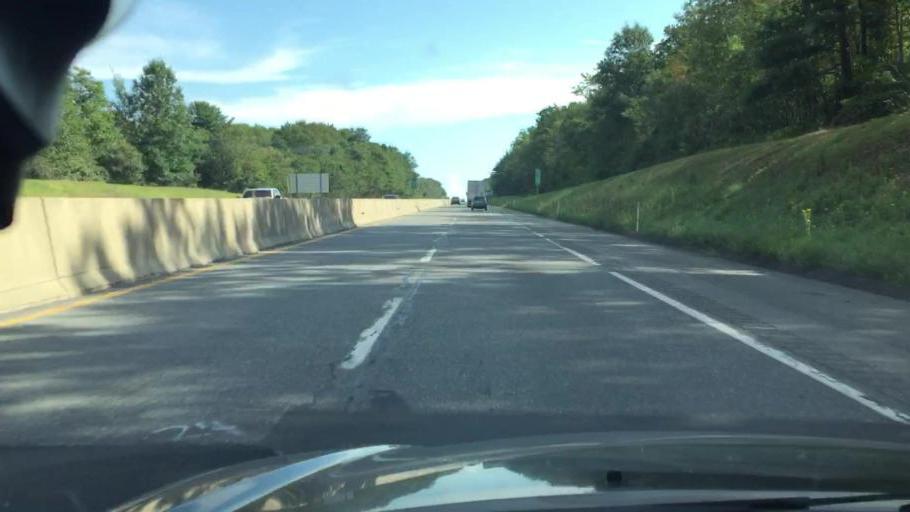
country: US
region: Pennsylvania
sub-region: Carbon County
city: Towamensing Trails
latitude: 40.9974
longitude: -75.6333
